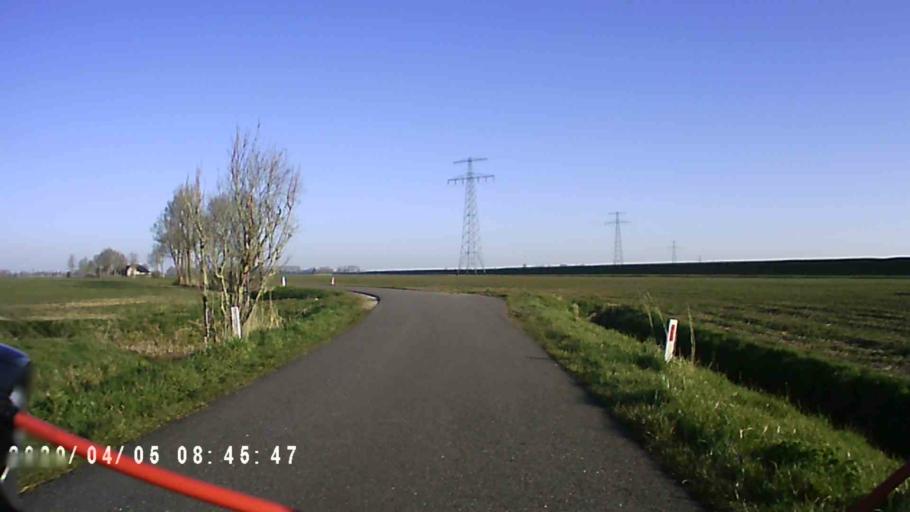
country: NL
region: Groningen
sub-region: Gemeente Winsum
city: Winsum
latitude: 53.3095
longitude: 6.4876
